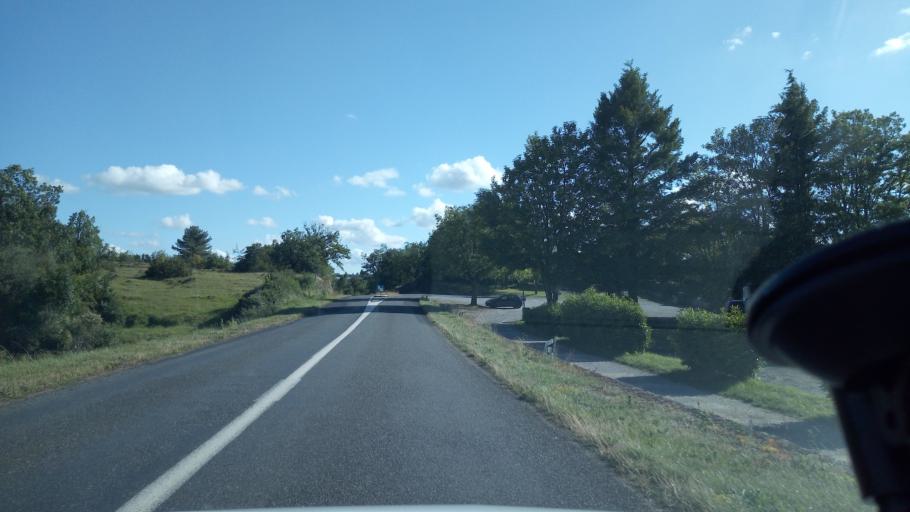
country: FR
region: Midi-Pyrenees
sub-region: Departement de l'Aveyron
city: Sebazac-Concoures
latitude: 44.4111
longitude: 2.6049
